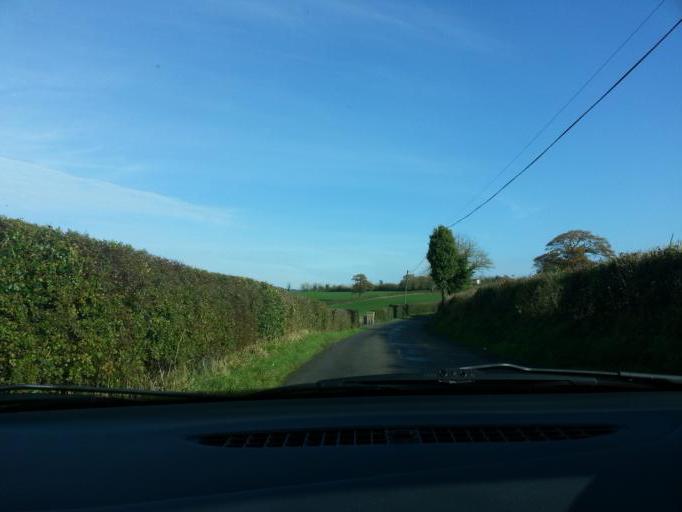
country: GB
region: Northern Ireland
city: Lisnaskea
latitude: 54.2483
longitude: -7.4127
